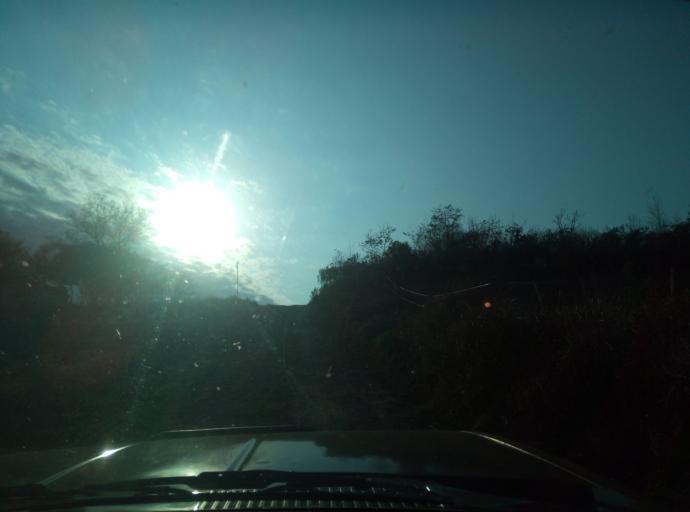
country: PY
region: Caaguazu
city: Doctor Cecilio Baez
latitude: -25.1990
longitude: -56.1186
